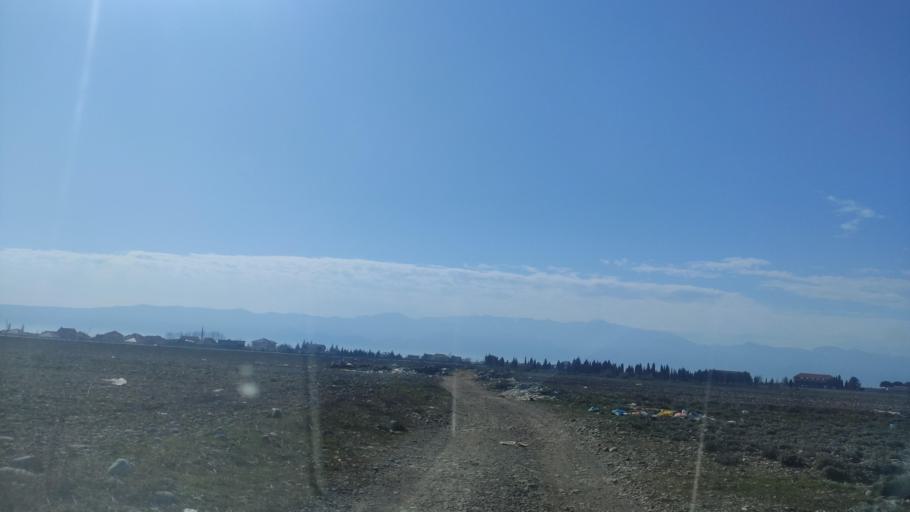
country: AL
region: Shkoder
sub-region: Rrethi i Malesia e Madhe
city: Koplik
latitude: 42.2252
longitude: 19.4358
